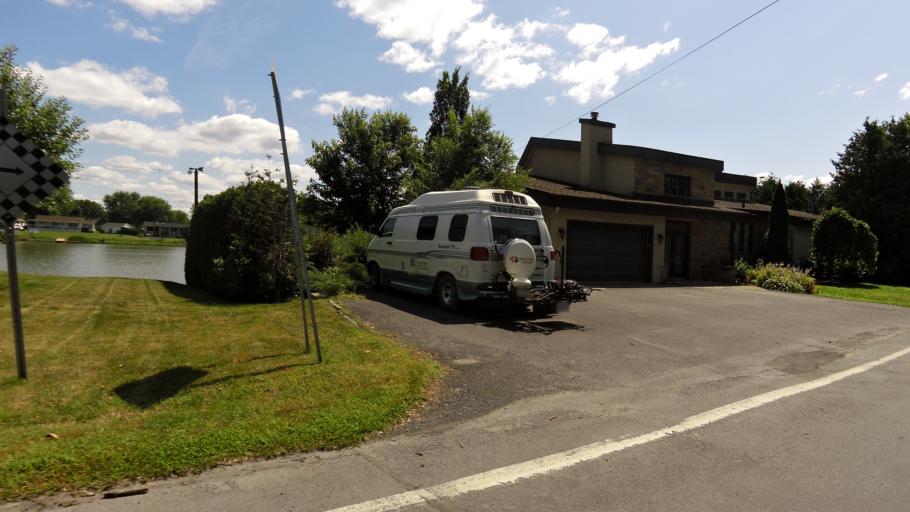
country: CA
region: Quebec
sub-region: Monteregie
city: Saint-Jean-sur-Richelieu
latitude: 45.3522
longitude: -73.2675
